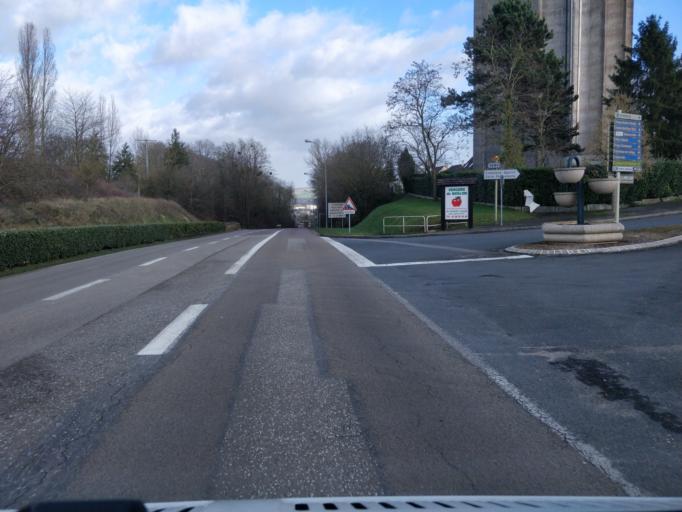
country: FR
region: Bourgogne
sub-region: Departement de l'Yonne
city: Paron
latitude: 48.1905
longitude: 3.2508
